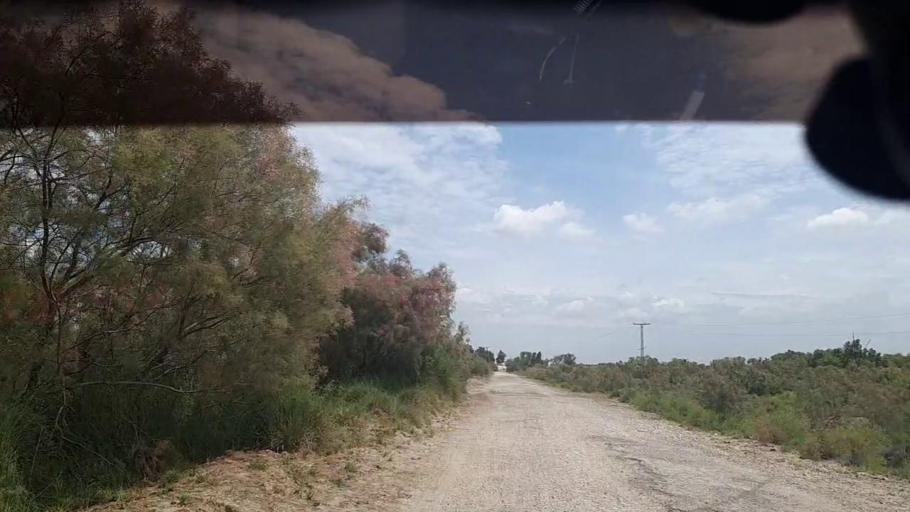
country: PK
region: Sindh
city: Rustam jo Goth
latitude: 28.0246
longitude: 68.9397
